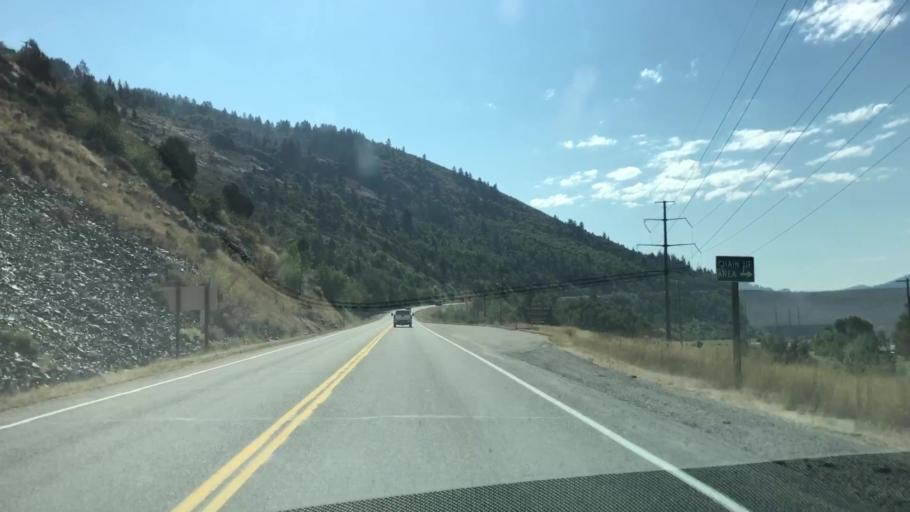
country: US
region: Idaho
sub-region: Teton County
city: Victor
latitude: 43.3450
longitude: -111.2069
